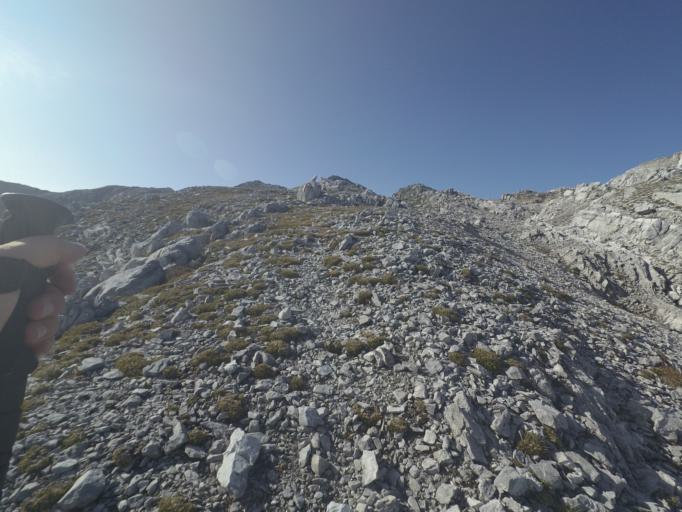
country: AT
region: Salzburg
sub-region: Politischer Bezirk Sankt Johann im Pongau
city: Kleinarl
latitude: 47.2158
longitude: 13.4023
